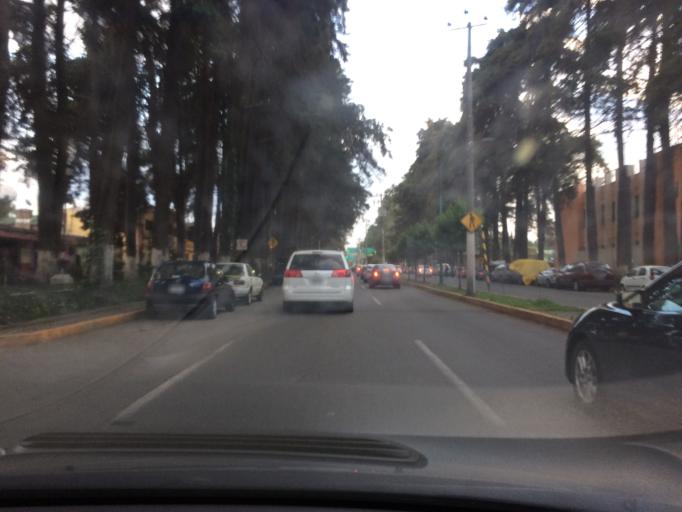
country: MX
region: Mexico
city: San Buenaventura
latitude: 19.2719
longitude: -99.6601
